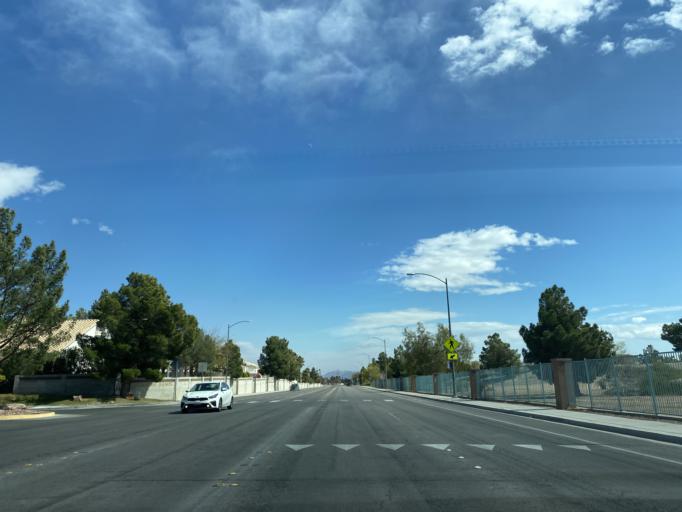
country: US
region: Nevada
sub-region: Clark County
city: Summerlin South
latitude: 36.2262
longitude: -115.2840
